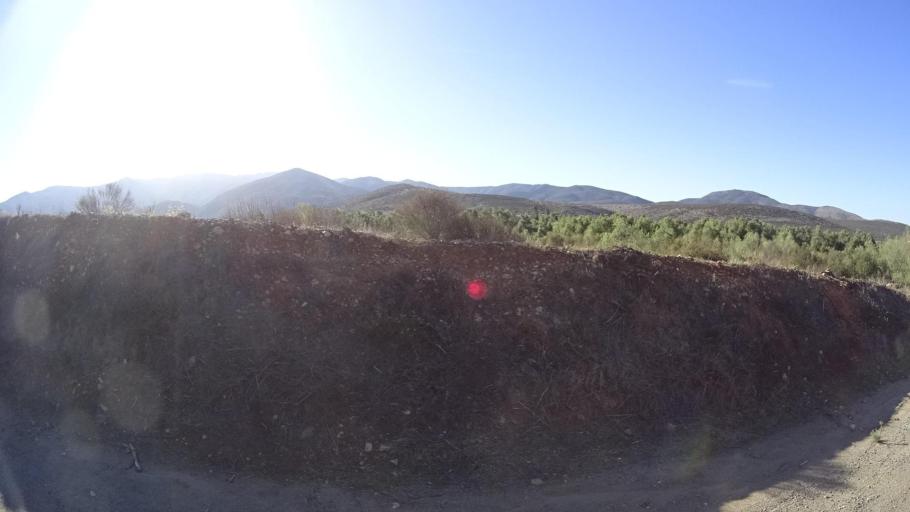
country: US
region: California
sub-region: San Diego County
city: Jamul
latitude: 32.6348
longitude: -116.8971
